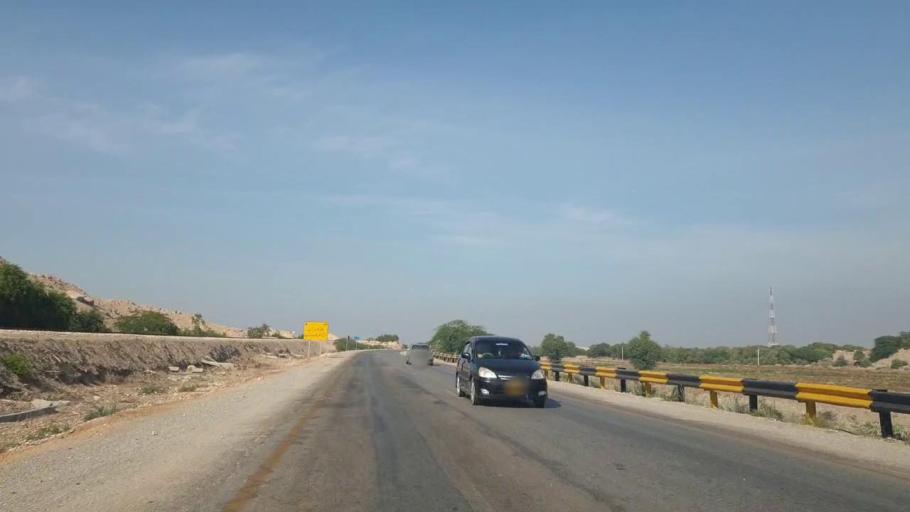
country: PK
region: Sindh
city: Sehwan
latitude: 26.2953
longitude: 67.8944
